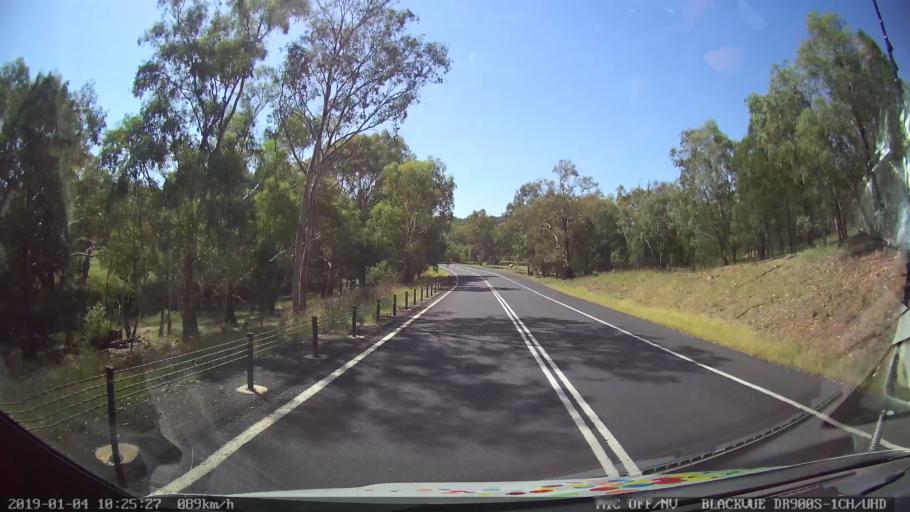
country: AU
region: New South Wales
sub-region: Cabonne
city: Canowindra
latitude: -33.3692
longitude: 148.5702
